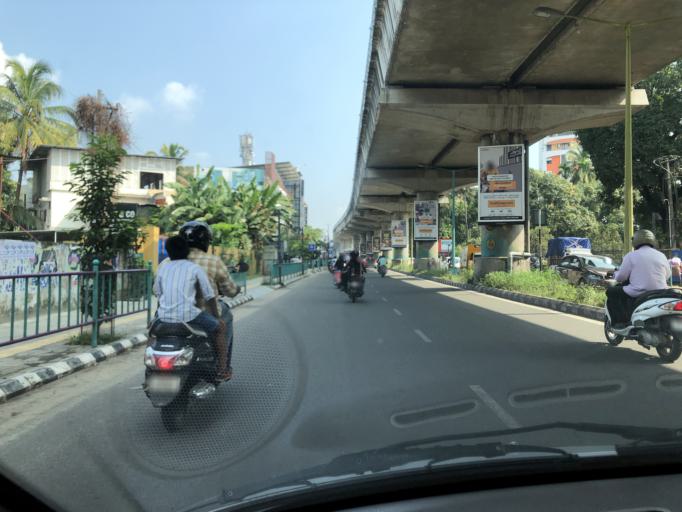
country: IN
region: Kerala
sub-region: Ernakulam
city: Elur
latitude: 10.0199
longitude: 76.3051
